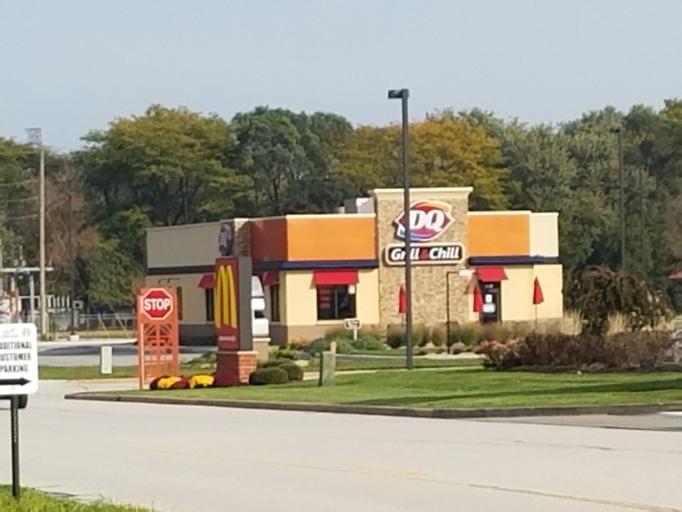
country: US
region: Indiana
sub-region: Porter County
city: Ogden Dunes
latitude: 41.6069
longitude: -87.1725
